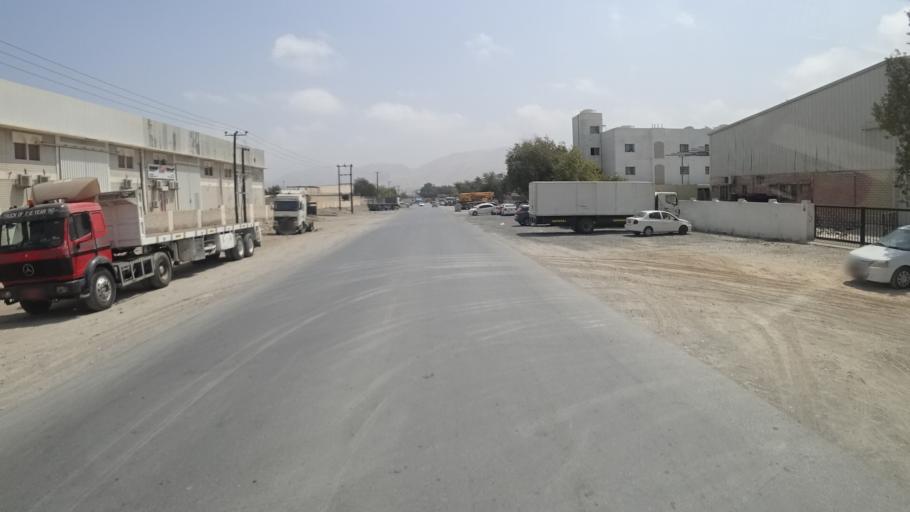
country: OM
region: Muhafazat Masqat
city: Bawshar
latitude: 23.5770
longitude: 58.3714
